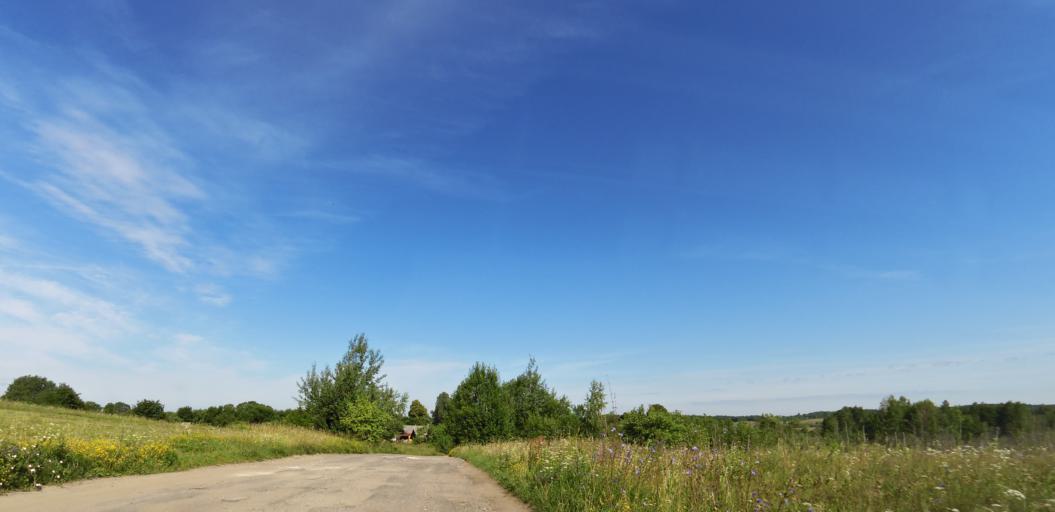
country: LT
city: Grigiskes
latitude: 54.7105
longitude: 25.0950
